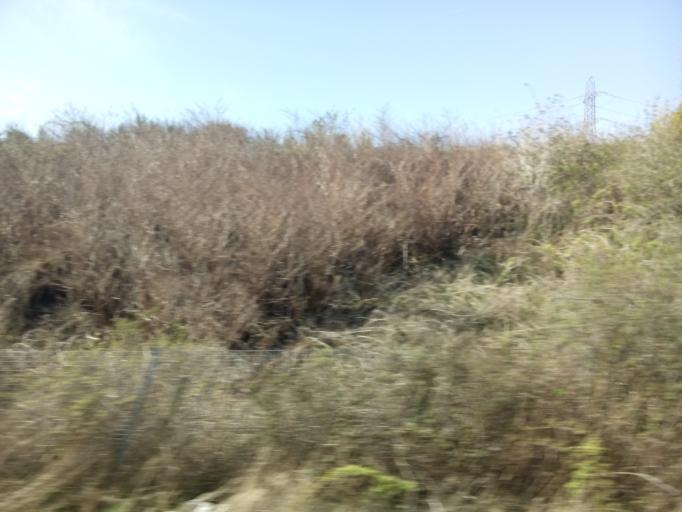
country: GB
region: Scotland
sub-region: East Lothian
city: Musselburgh
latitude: 55.9365
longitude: -3.0805
